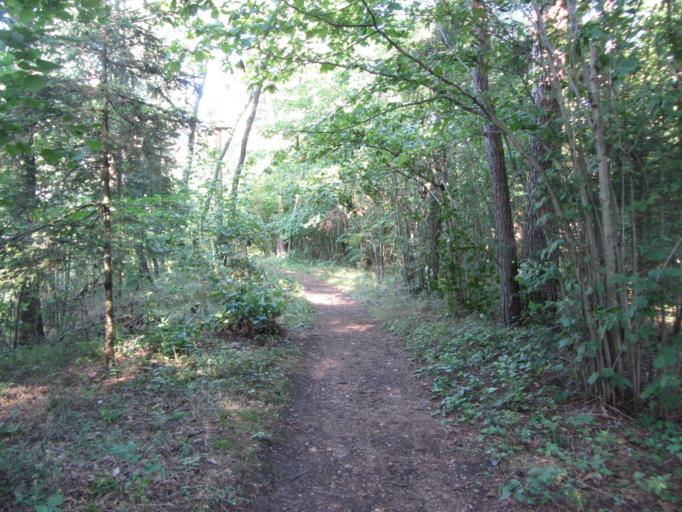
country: LT
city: Birstonas
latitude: 54.6050
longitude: 24.0056
